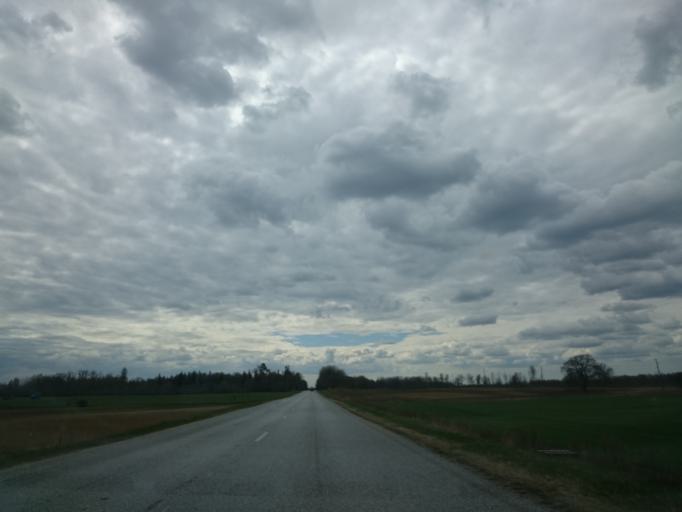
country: LV
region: Aizpute
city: Aizpute
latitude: 56.8196
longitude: 21.7294
